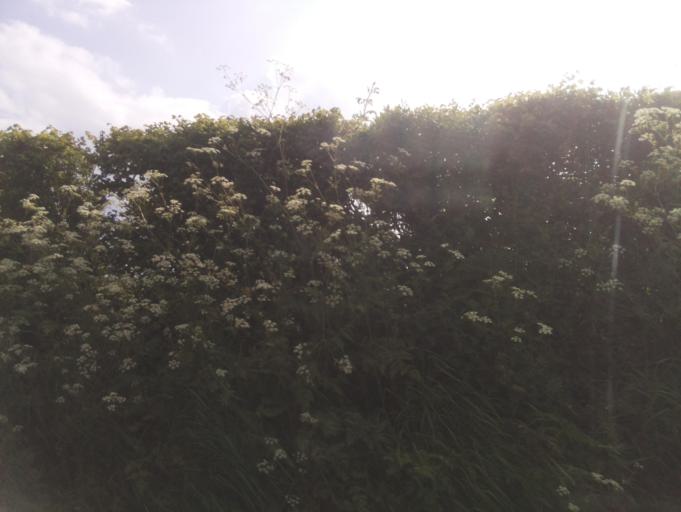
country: GB
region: England
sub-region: Wiltshire
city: Malmesbury
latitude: 51.5536
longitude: -2.1066
